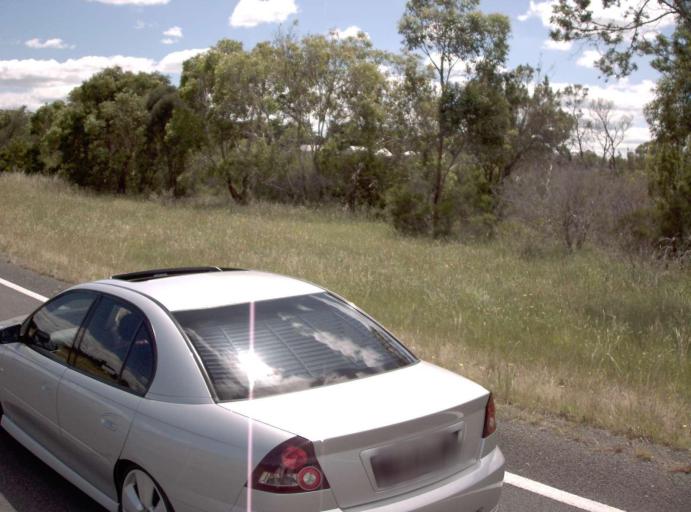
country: AU
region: Victoria
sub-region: Cardinia
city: Koo-Wee-Rup
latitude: -38.2950
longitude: 145.5444
